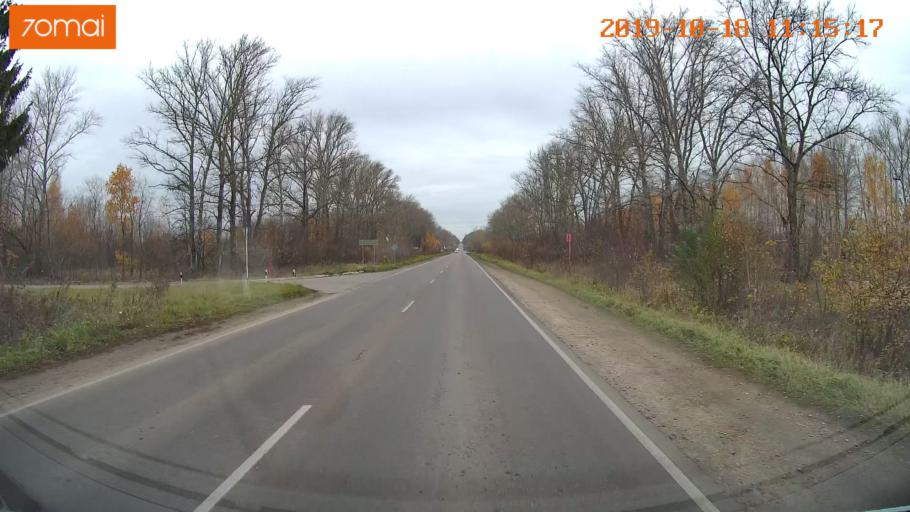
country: RU
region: Tula
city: Kimovsk
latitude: 53.9910
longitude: 38.5474
